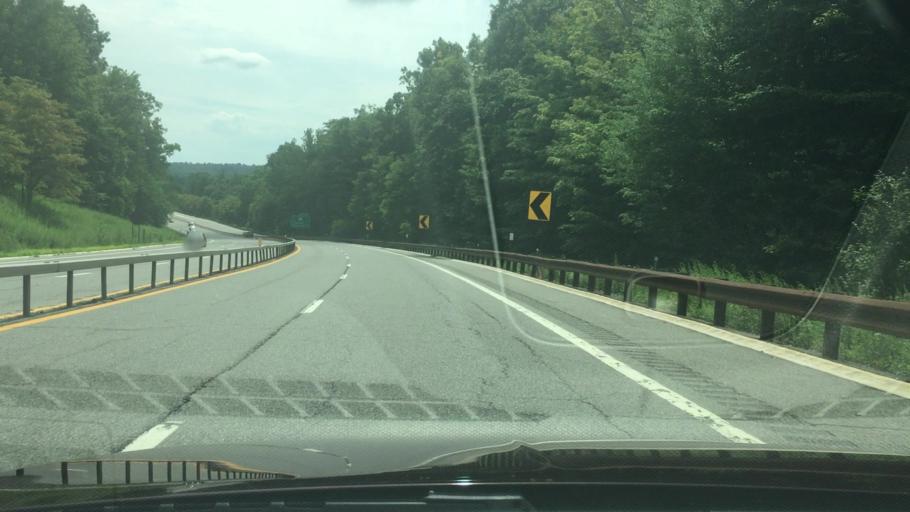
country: US
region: New York
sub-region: Westchester County
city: Shrub Oak
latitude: 41.3397
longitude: -73.8153
